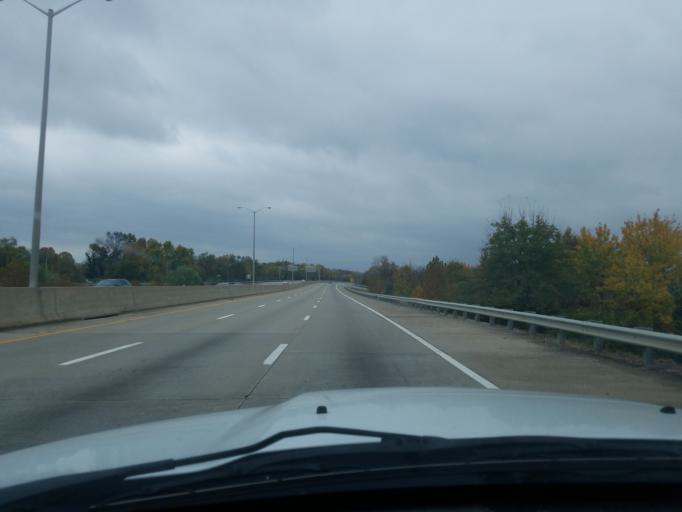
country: US
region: Kentucky
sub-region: Jefferson County
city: Shively
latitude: 38.2062
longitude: -85.8280
